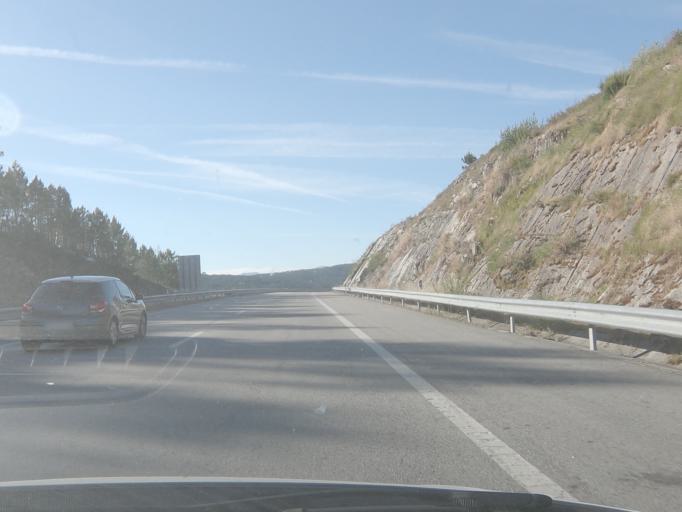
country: PT
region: Viseu
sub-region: Castro Daire
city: Castro Daire
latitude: 40.8296
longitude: -7.9366
